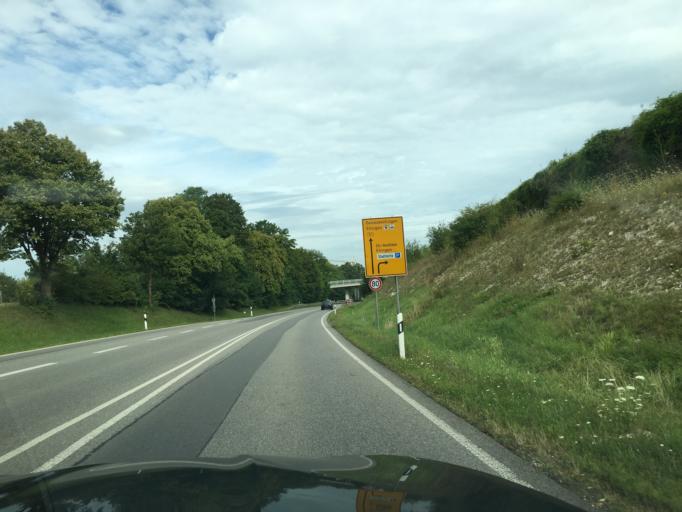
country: DE
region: Baden-Wuerttemberg
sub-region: Tuebingen Region
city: Ehingen
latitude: 48.2853
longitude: 9.7381
